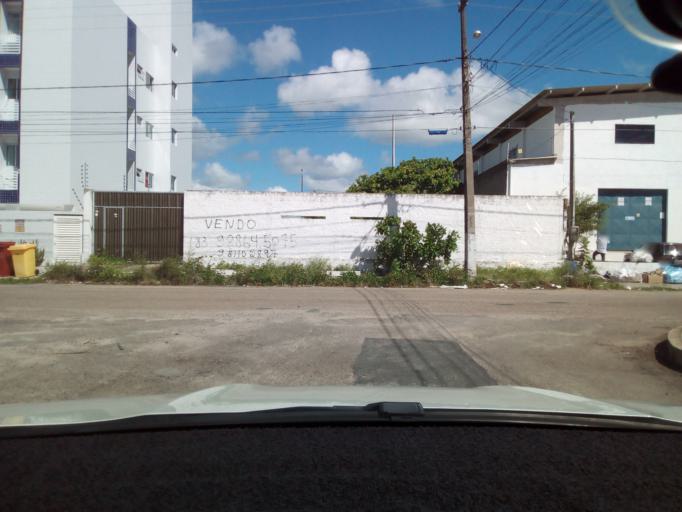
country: BR
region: Paraiba
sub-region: Joao Pessoa
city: Joao Pessoa
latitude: -7.0522
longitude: -34.8490
